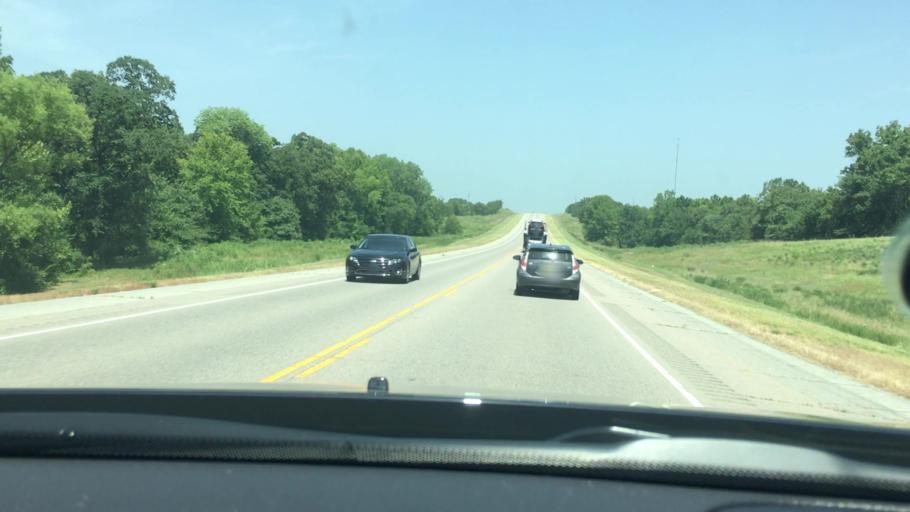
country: US
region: Oklahoma
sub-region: Pontotoc County
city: Ada
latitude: 34.6293
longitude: -96.4672
